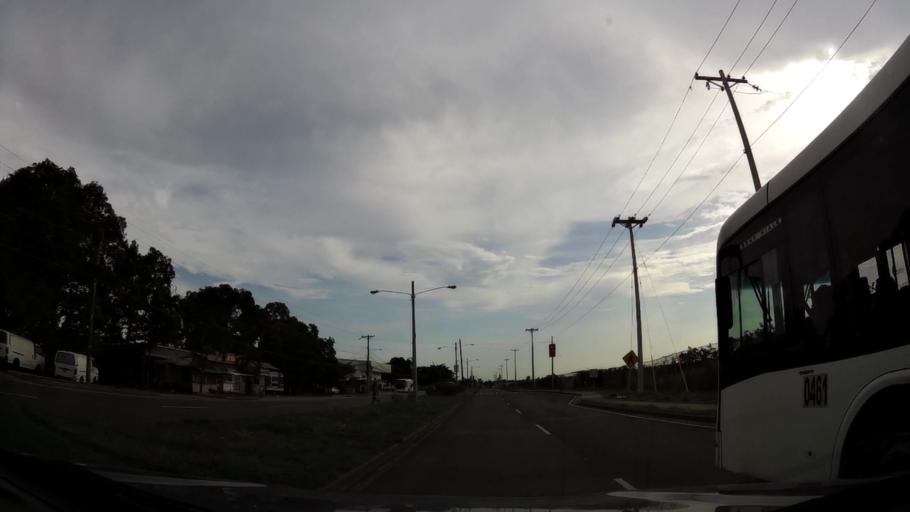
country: PA
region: Panama
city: Tocumen
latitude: 9.0843
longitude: -79.3666
